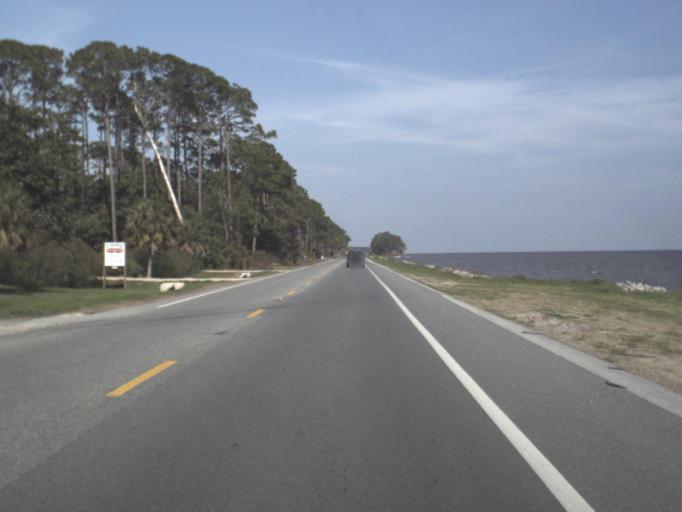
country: US
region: Florida
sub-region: Franklin County
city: Eastpoint
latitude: 29.7465
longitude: -84.8592
